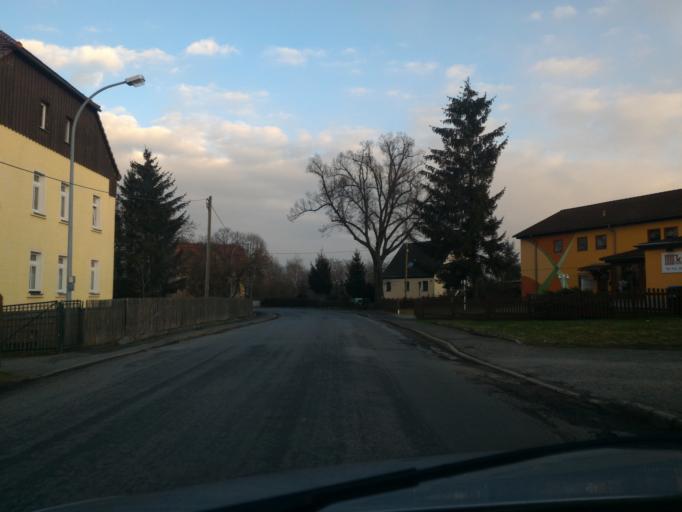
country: DE
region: Saxony
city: Mittelherwigsdorf
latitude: 50.9219
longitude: 14.7412
